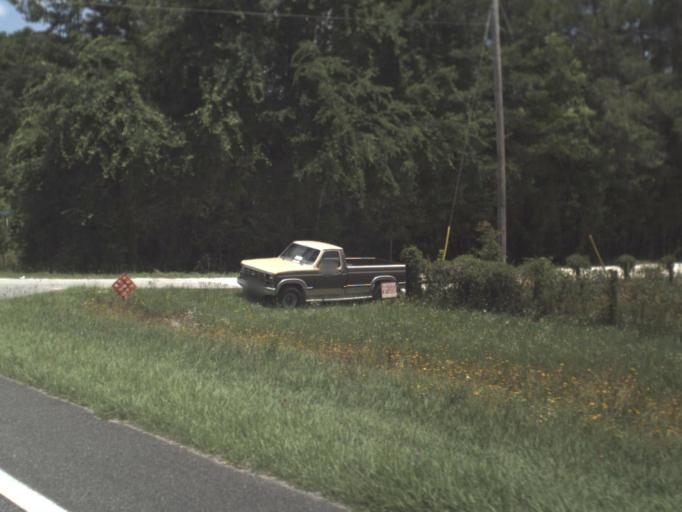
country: US
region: Florida
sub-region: Alachua County
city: High Springs
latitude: 29.8896
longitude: -82.6735
